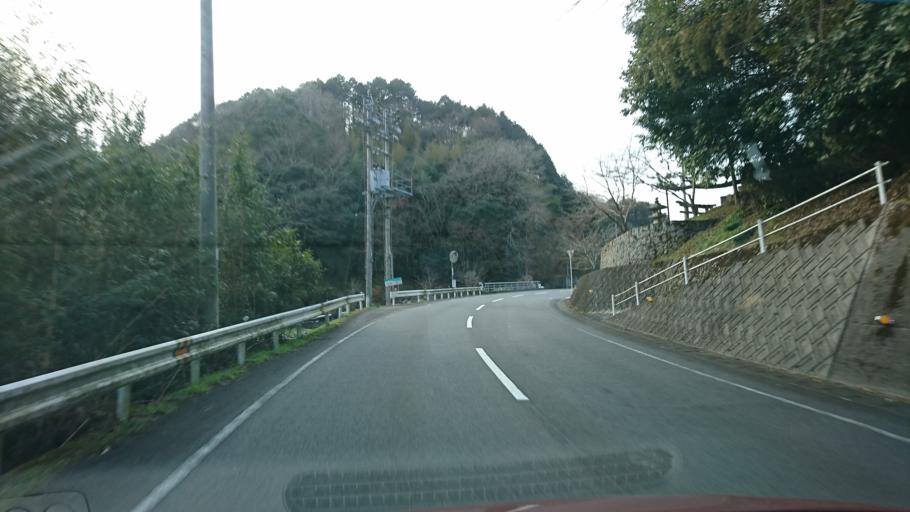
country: JP
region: Ehime
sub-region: Shikoku-chuo Shi
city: Matsuyama
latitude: 33.8993
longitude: 132.8266
